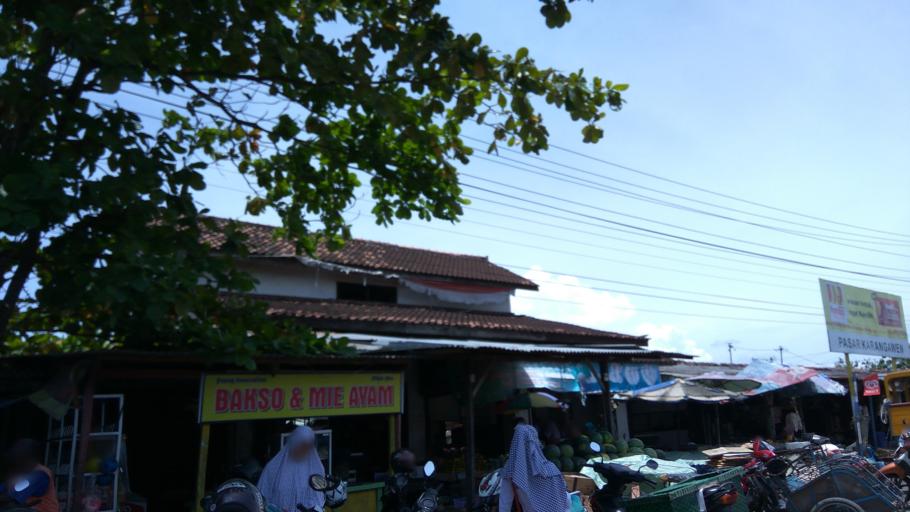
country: ID
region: Central Java
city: Mranggen
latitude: -7.0449
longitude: 110.5783
